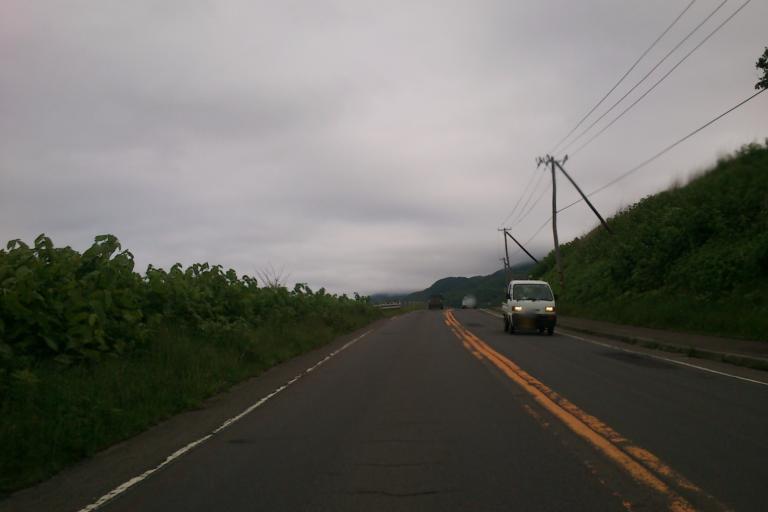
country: JP
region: Hokkaido
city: Ishikari
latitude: 43.4051
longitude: 141.4306
